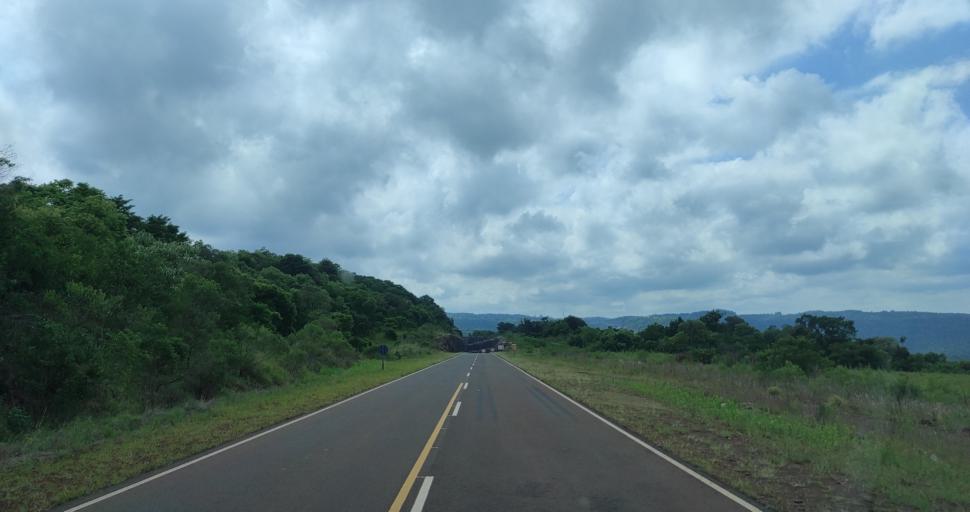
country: AR
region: Misiones
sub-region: Departamento de Veinticinco de Mayo
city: Veinticinco de Mayo
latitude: -27.3768
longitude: -54.8451
